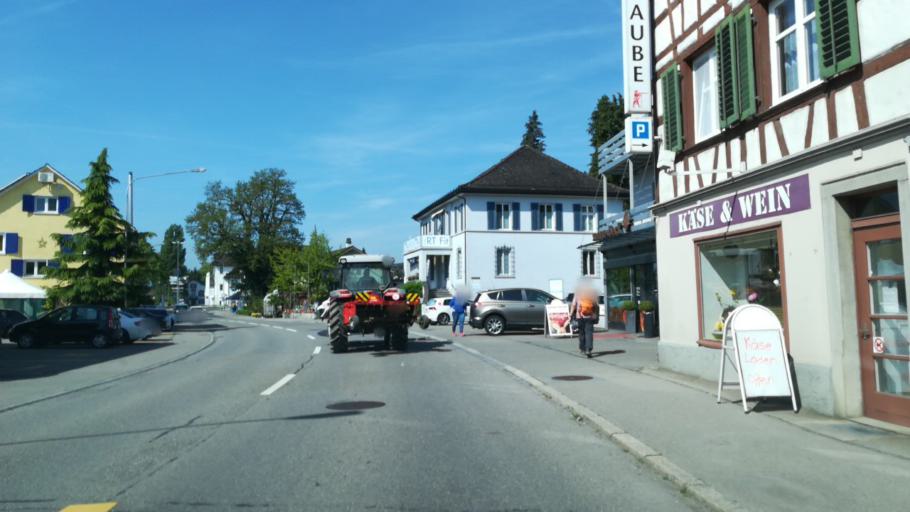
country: CH
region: Thurgau
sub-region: Frauenfeld District
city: Mullheim
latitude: 47.6029
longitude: 9.0034
